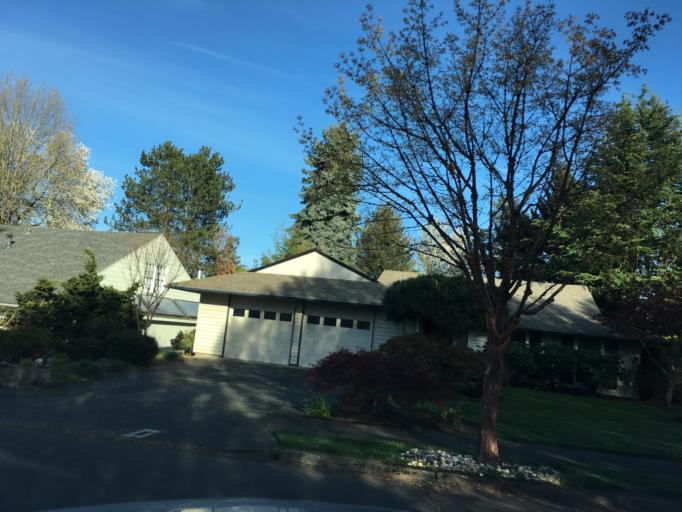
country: US
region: Oregon
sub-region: Multnomah County
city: Lents
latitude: 45.5503
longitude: -122.5240
